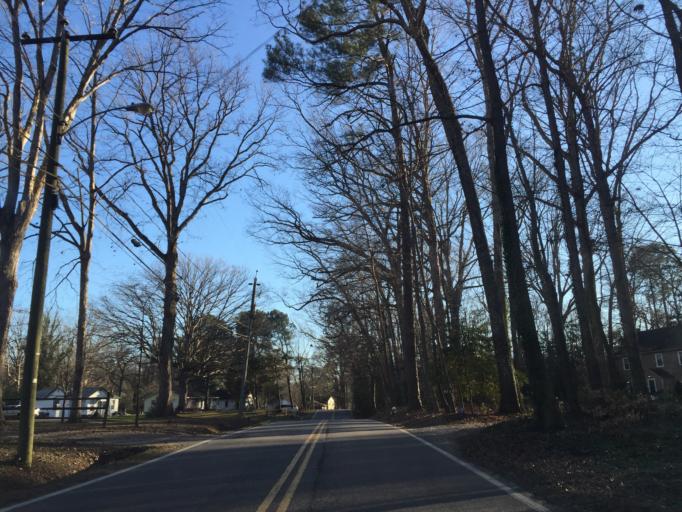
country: US
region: Virginia
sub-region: City of Newport News
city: Newport News
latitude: 37.0868
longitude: -76.5117
